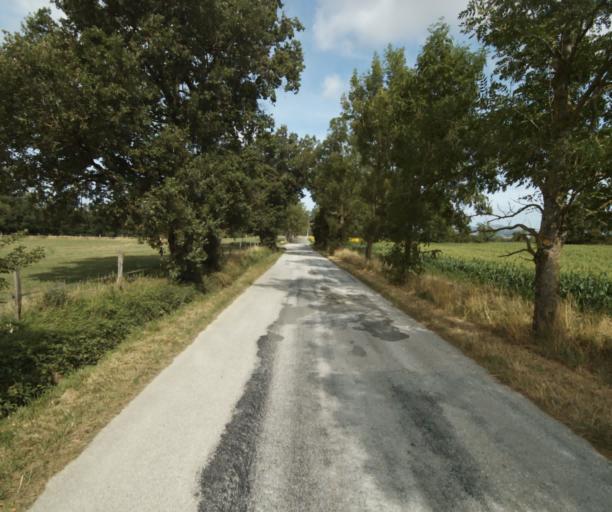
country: FR
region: Midi-Pyrenees
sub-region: Departement du Tarn
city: Dourgne
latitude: 43.4686
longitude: 2.1048
